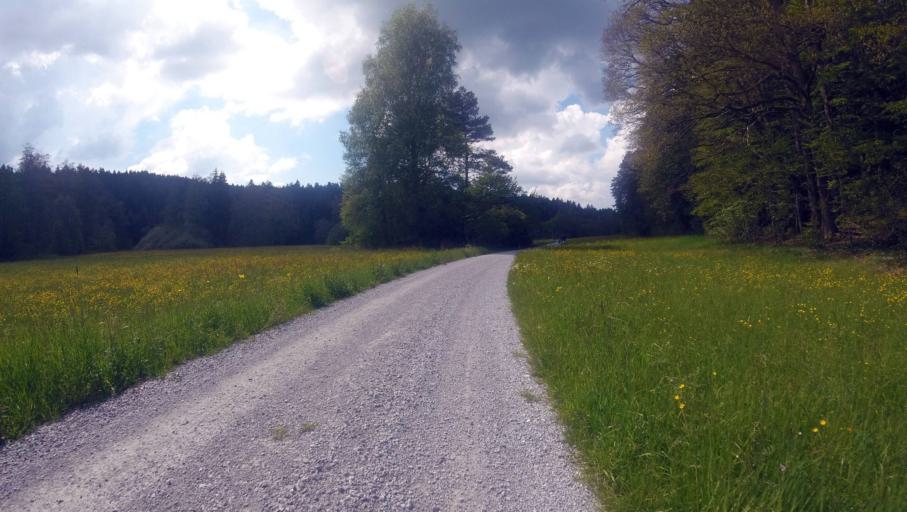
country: DE
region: Baden-Wuerttemberg
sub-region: Regierungsbezirk Stuttgart
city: Spraitbach
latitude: 48.8579
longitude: 9.7606
